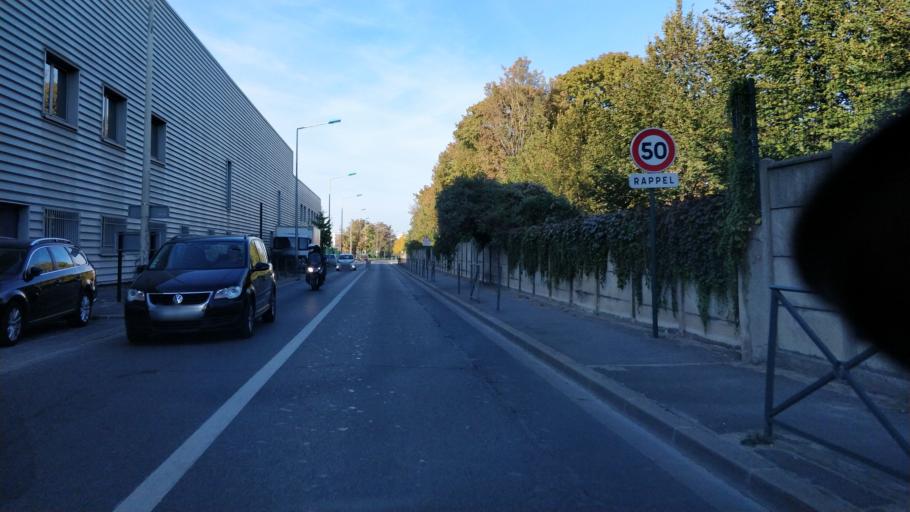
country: FR
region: Ile-de-France
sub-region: Departement des Hauts-de-Seine
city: Bagneux
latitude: 48.8034
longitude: 2.3030
